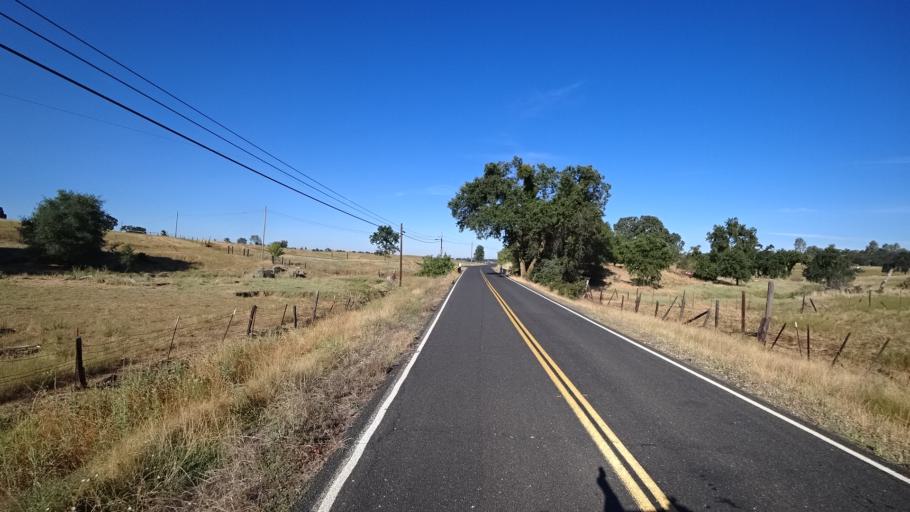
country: US
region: California
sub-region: Calaveras County
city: Valley Springs
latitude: 38.1933
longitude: -120.8056
